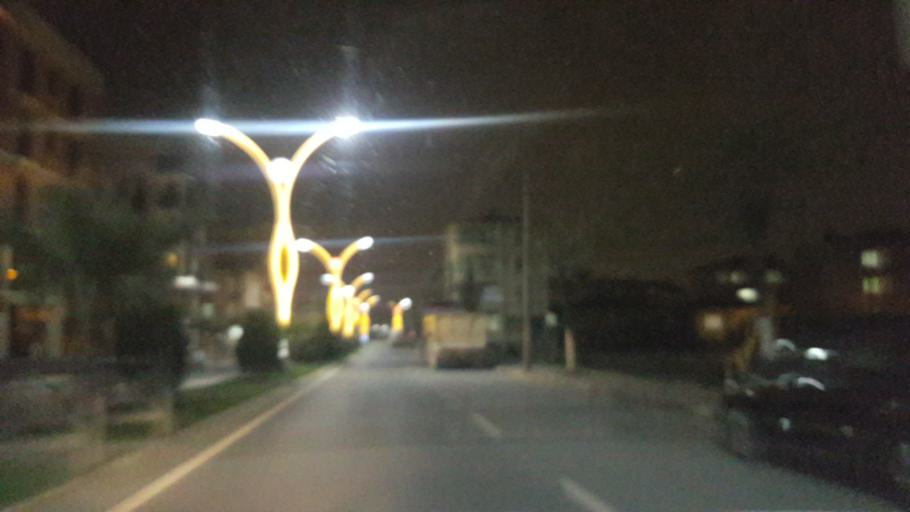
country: TR
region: Kocaeli
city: Darica
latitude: 40.7792
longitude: 29.4014
